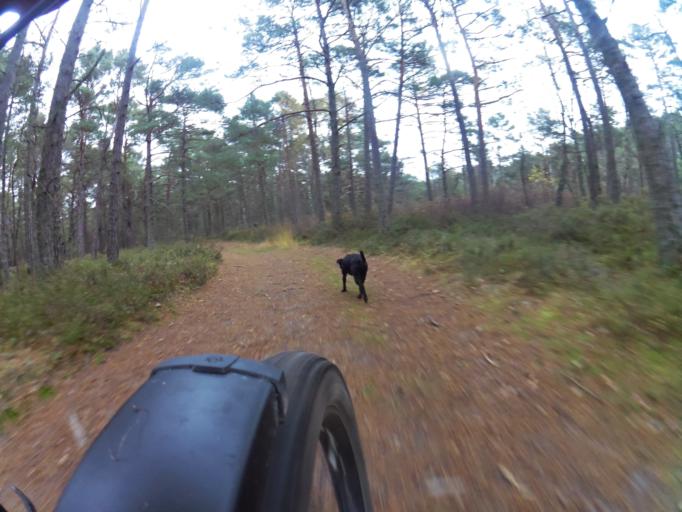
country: PL
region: Pomeranian Voivodeship
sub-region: Powiat leborski
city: Leba
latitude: 54.7768
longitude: 17.6911
